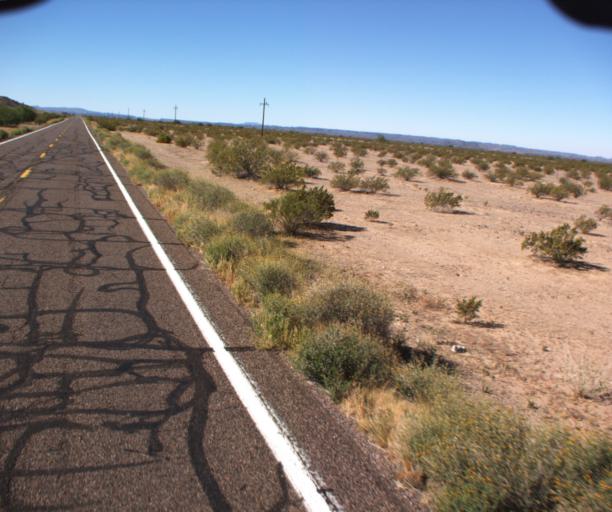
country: US
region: Arizona
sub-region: Maricopa County
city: Gila Bend
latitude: 32.7047
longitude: -112.8469
